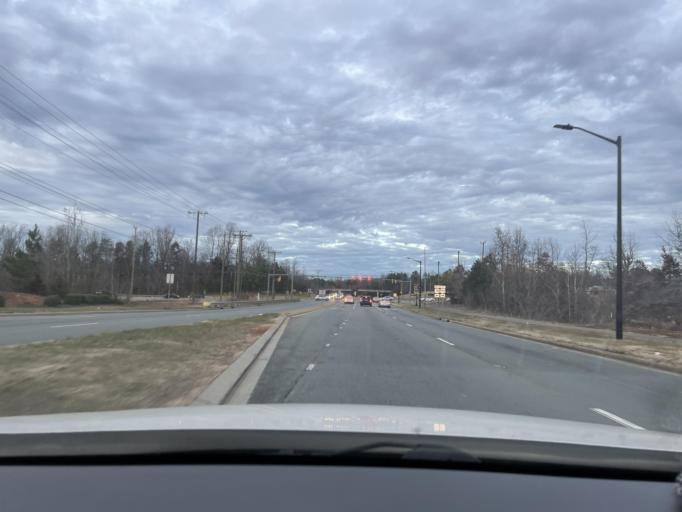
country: US
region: North Carolina
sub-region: Guilford County
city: Gibsonville
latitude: 36.0791
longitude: -79.5273
